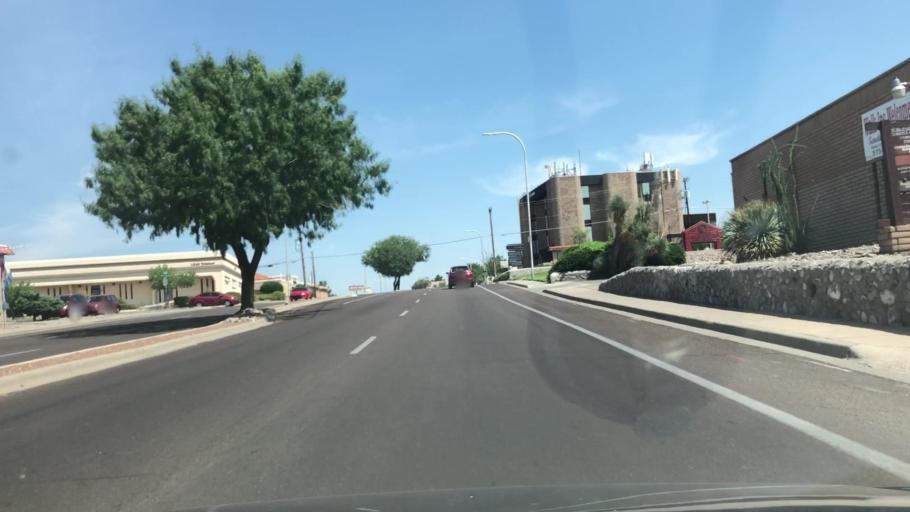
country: US
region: New Mexico
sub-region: Dona Ana County
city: University Park
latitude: 32.3044
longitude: -106.7380
